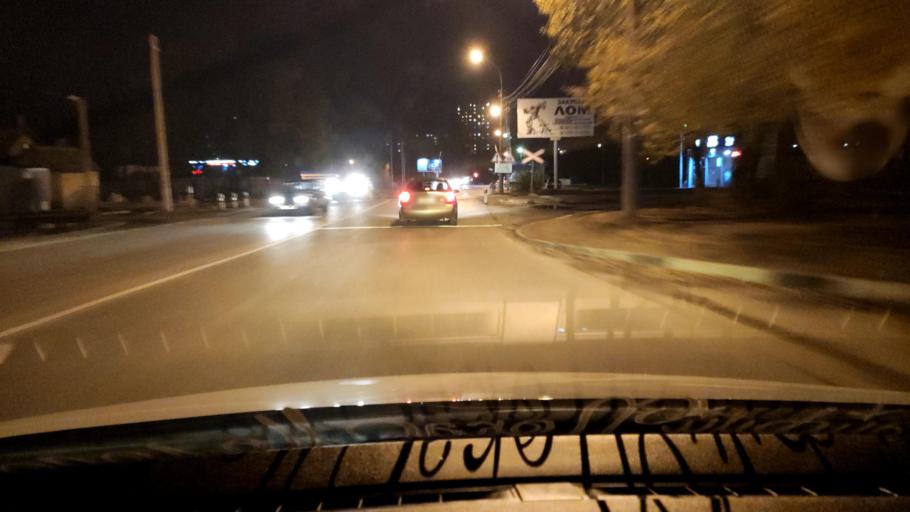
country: RU
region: Voronezj
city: Voronezh
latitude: 51.6664
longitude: 39.1507
